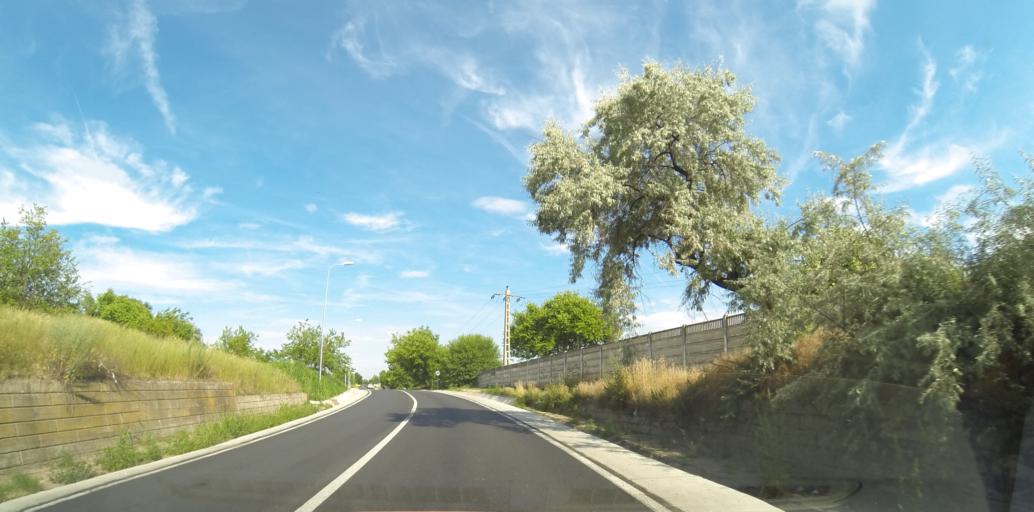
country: RO
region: Dolj
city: Craiova
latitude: 44.3424
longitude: 23.7897
